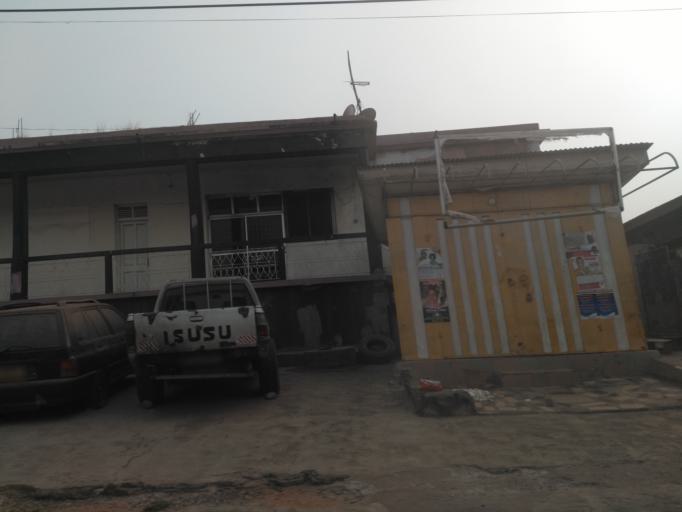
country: GH
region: Ashanti
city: Kumasi
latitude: 6.7081
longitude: -1.6226
